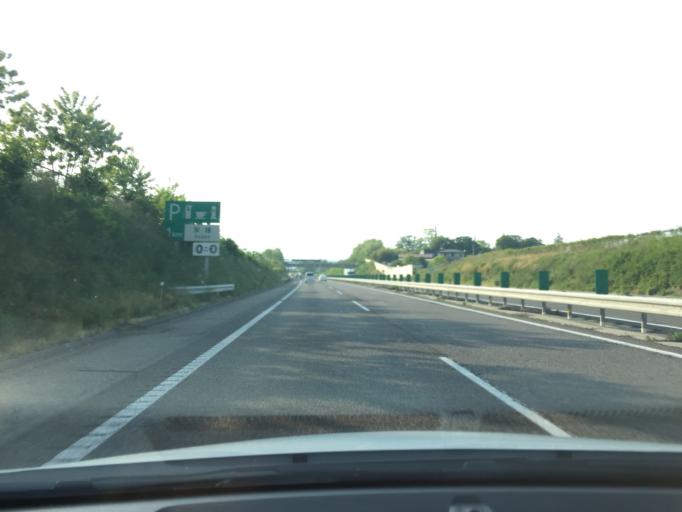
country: JP
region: Fukushima
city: Koriyama
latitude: 37.3454
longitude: 140.3313
